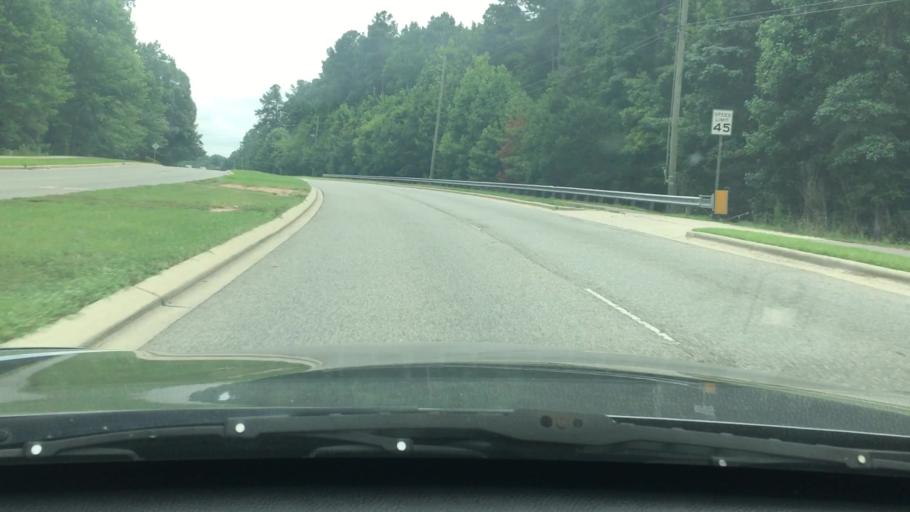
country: US
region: North Carolina
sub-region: Wake County
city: West Raleigh
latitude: 35.8414
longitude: -78.7147
